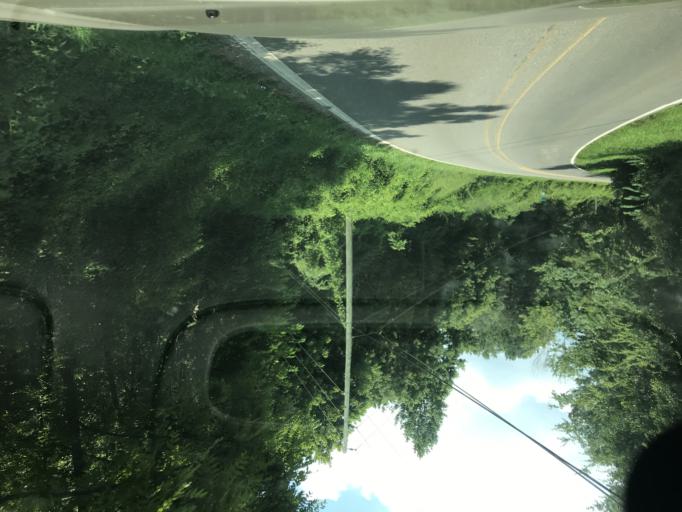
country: US
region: Georgia
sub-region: Dawson County
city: Dawsonville
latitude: 34.3289
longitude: -84.1759
